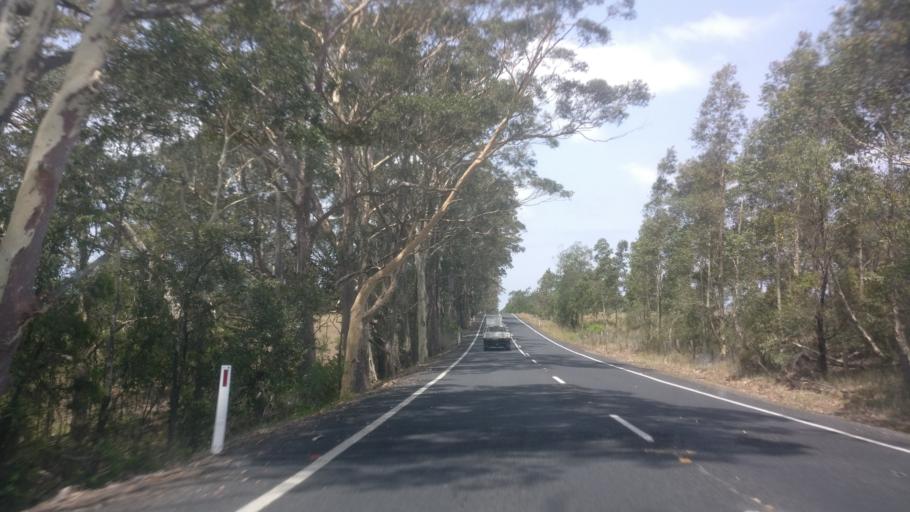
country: AU
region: New South Wales
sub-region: Shoalhaven Shire
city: Bomaderry
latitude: -34.8269
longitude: 150.5741
